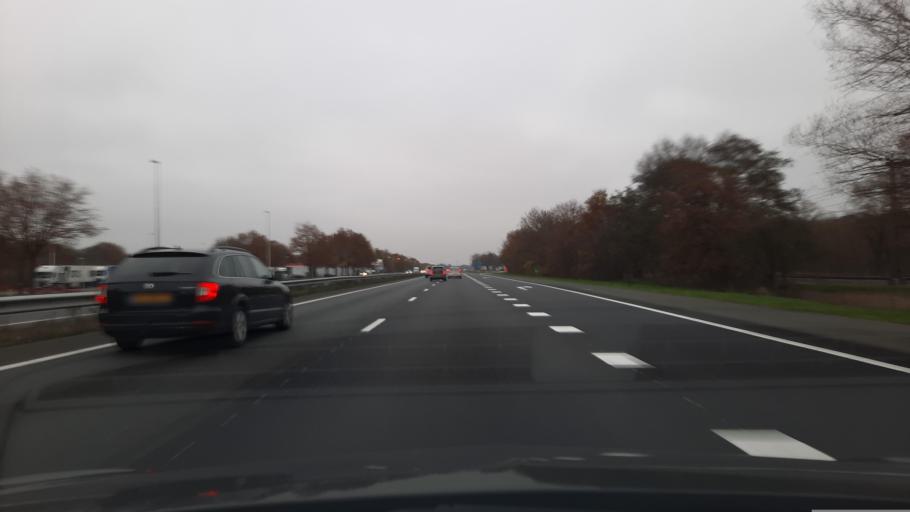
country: NL
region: Gelderland
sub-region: Gemeente Barneveld
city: Stroe
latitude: 52.1830
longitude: 5.6699
